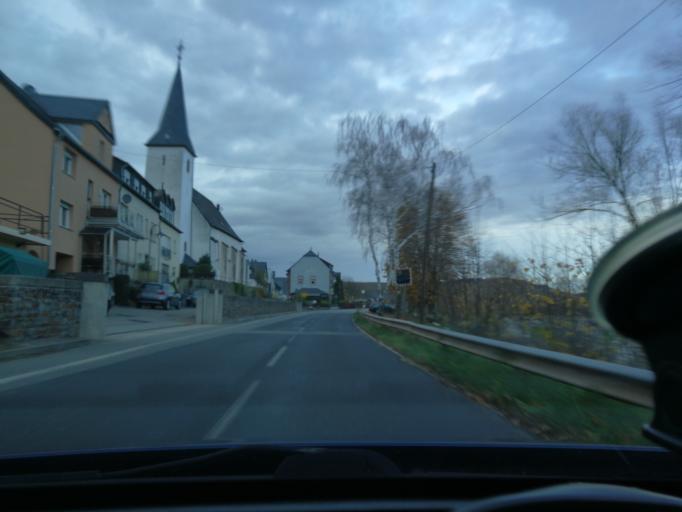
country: DE
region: Rheinland-Pfalz
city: Kesten
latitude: 49.8987
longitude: 6.9538
